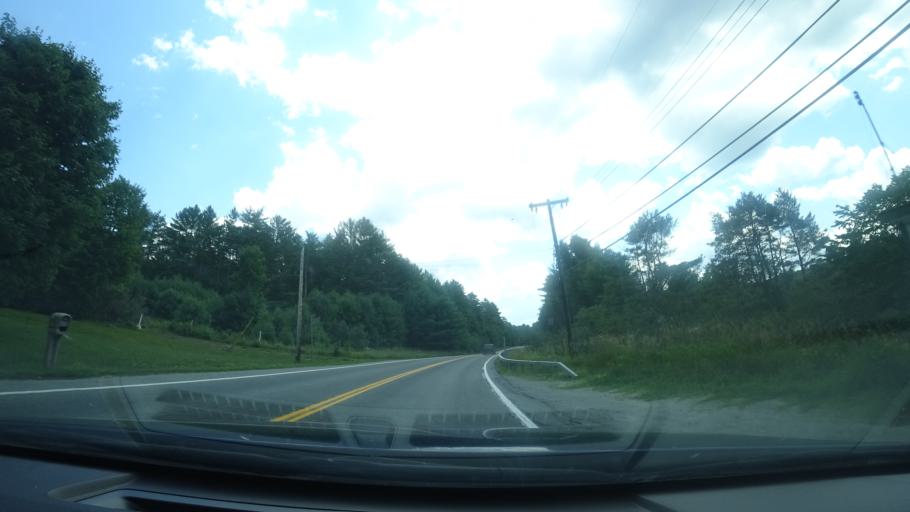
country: US
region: New York
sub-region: Warren County
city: Warrensburg
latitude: 43.6601
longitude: -73.8173
